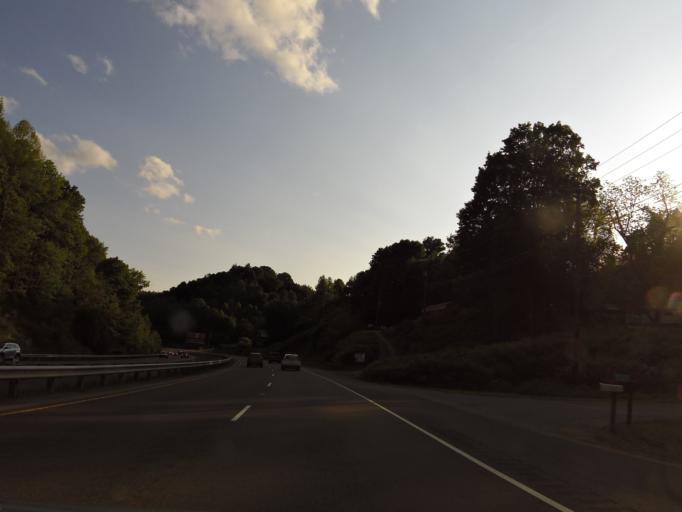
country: US
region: Virginia
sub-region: Russell County
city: Lebanon
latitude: 36.9228
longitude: -82.0031
